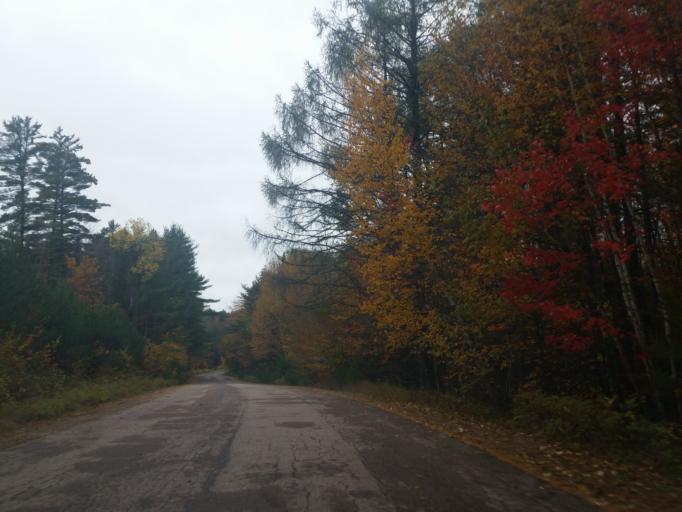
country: CA
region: Ontario
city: Deep River
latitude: 45.9952
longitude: -77.4141
